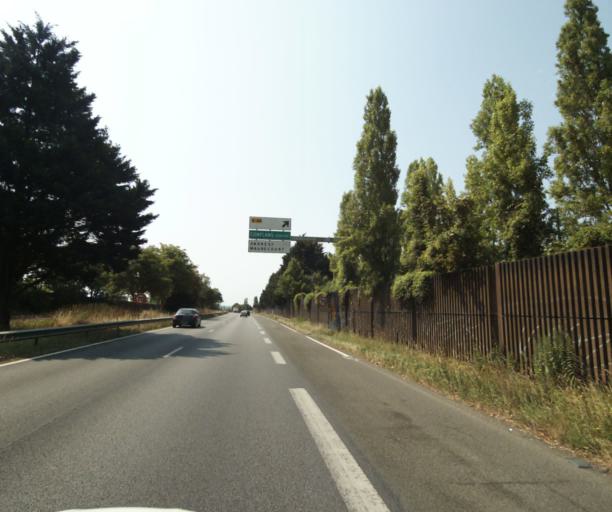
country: FR
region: Ile-de-France
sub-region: Departement des Yvelines
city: Conflans-Sainte-Honorine
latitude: 48.9944
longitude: 2.0807
